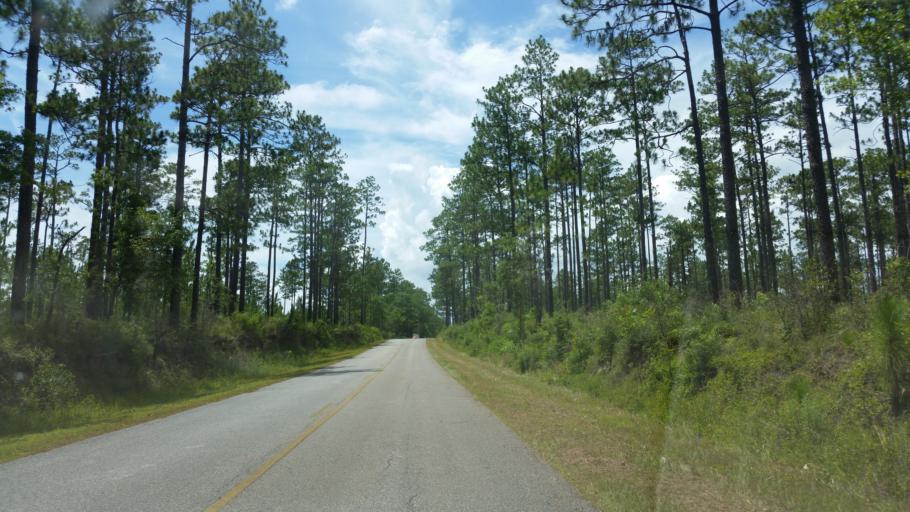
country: US
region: Florida
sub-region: Okaloosa County
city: Crestview
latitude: 30.7273
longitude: -86.7989
